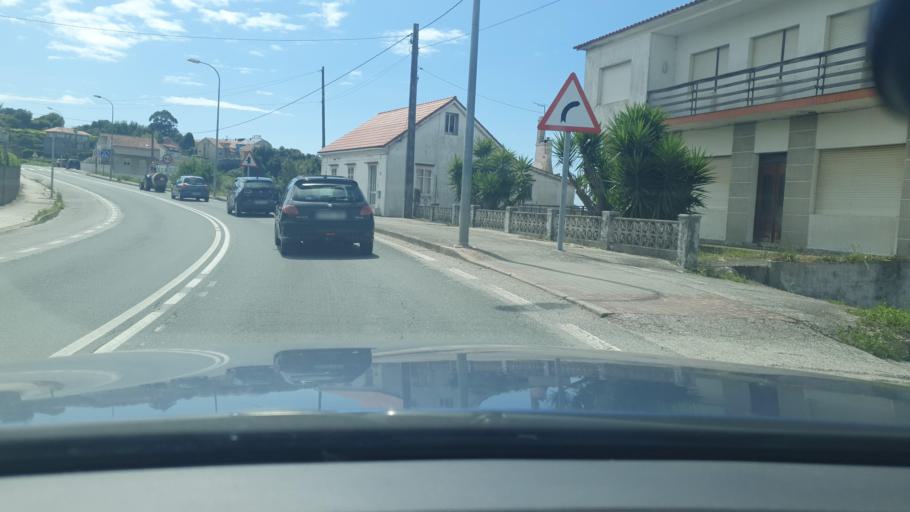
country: ES
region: Galicia
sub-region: Provincia de Pontevedra
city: Sanxenxo
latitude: 42.4411
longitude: -8.8410
